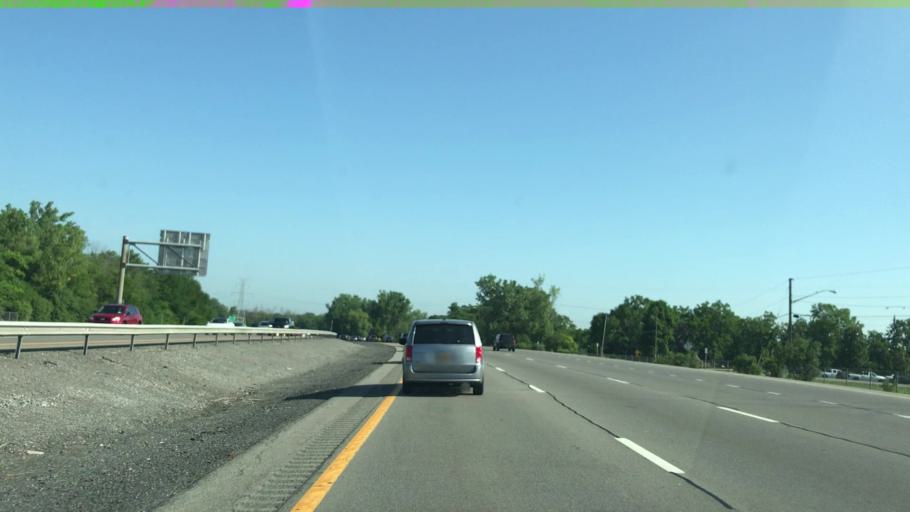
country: US
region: New York
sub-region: Erie County
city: Williamsville
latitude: 42.9634
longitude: -78.7671
